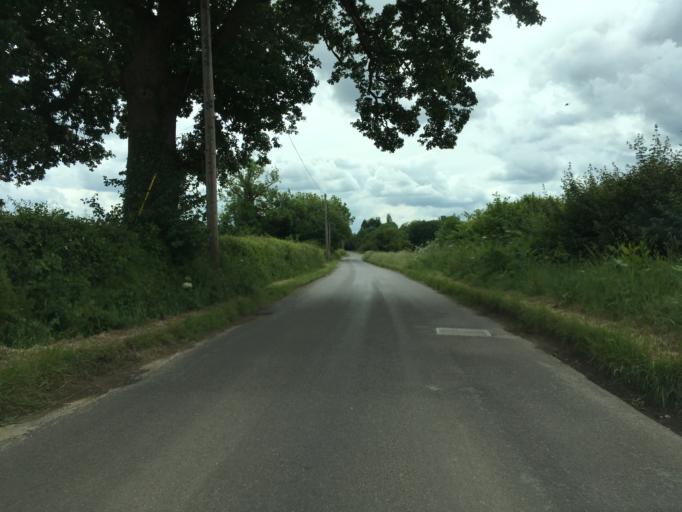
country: GB
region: England
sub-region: Wiltshire
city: Charlton
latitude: 51.5513
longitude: -2.0508
